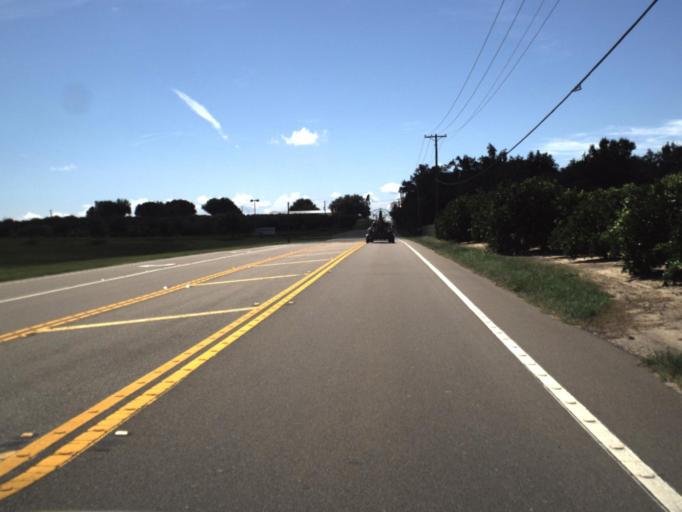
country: US
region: Florida
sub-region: Polk County
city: Frostproof
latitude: 27.7276
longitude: -81.5310
